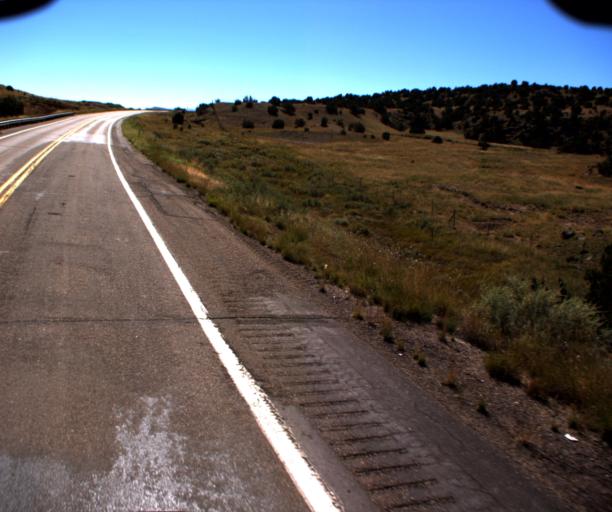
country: US
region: Arizona
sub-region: Apache County
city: Saint Johns
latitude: 34.3589
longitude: -109.3815
